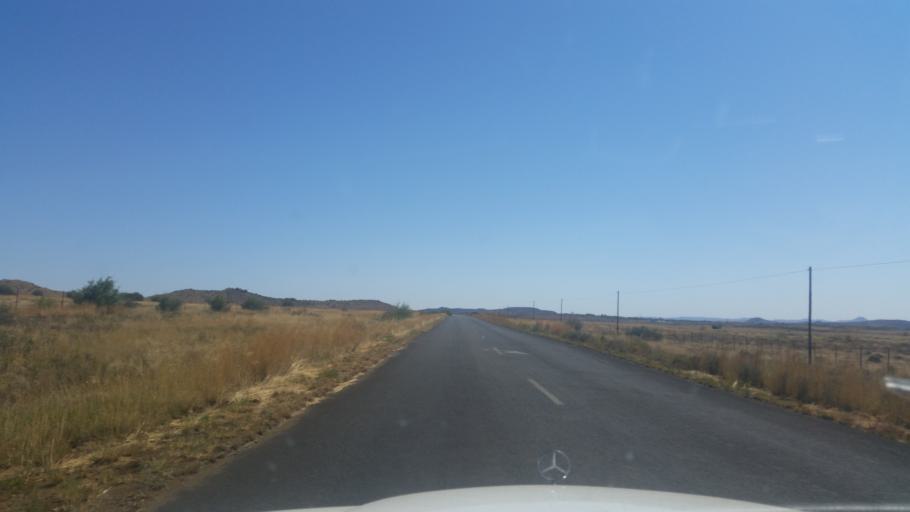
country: ZA
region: Eastern Cape
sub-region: Joe Gqabi District Municipality
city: Burgersdorp
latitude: -30.7371
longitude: 25.7545
